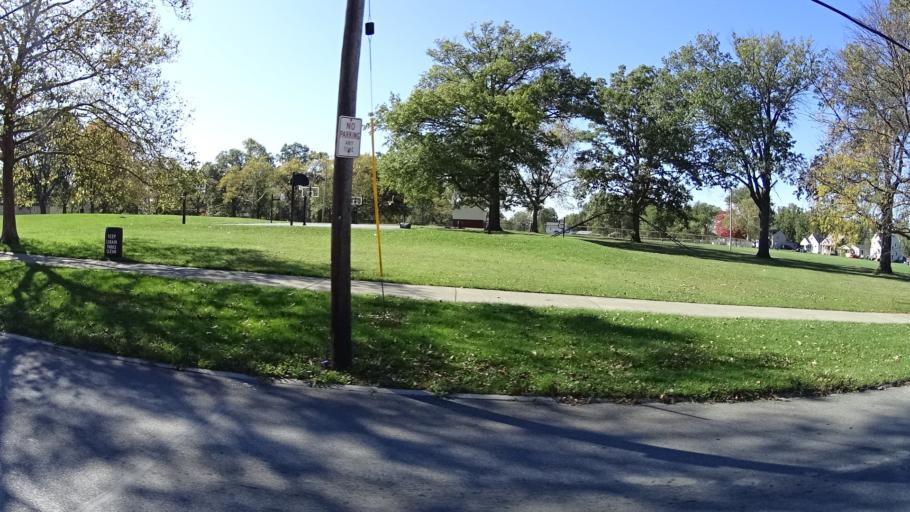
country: US
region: Ohio
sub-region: Lorain County
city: Lorain
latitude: 41.4448
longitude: -82.1718
